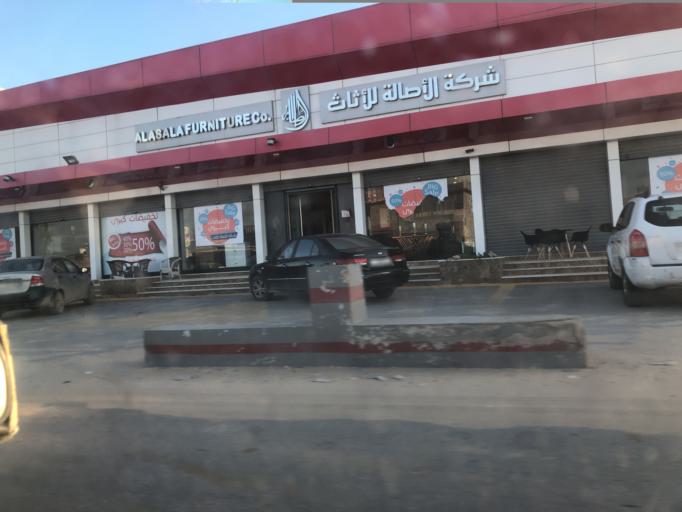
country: LY
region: Tripoli
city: Tagiura
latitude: 32.8662
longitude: 13.2793
